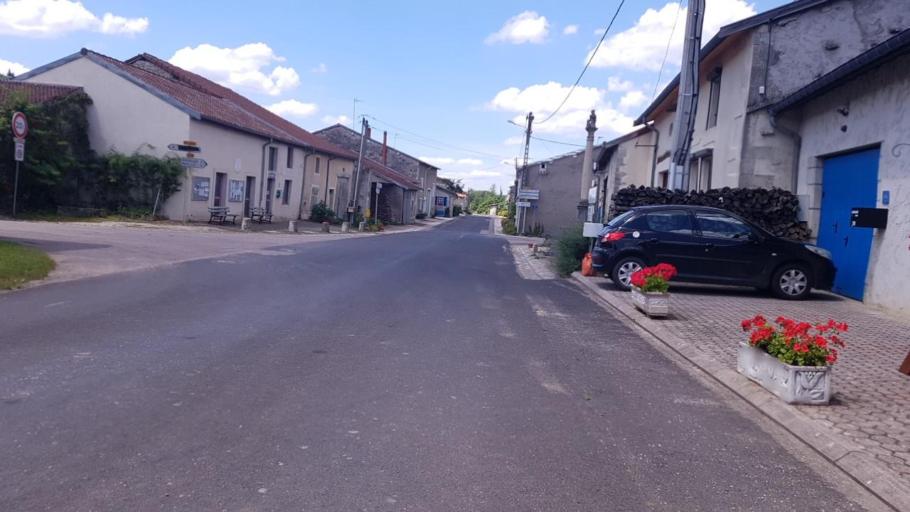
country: FR
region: Lorraine
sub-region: Departement de la Meuse
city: Ligny-en-Barrois
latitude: 48.6413
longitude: 5.4456
